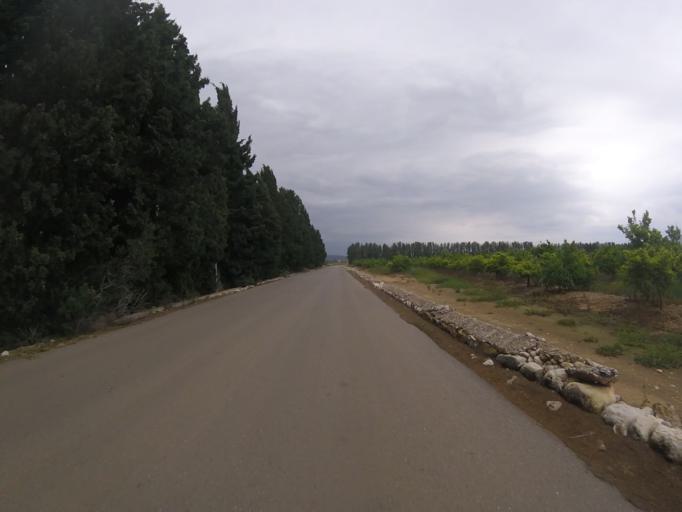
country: ES
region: Valencia
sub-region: Provincia de Castello
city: Alcoceber
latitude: 40.2104
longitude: 0.2514
